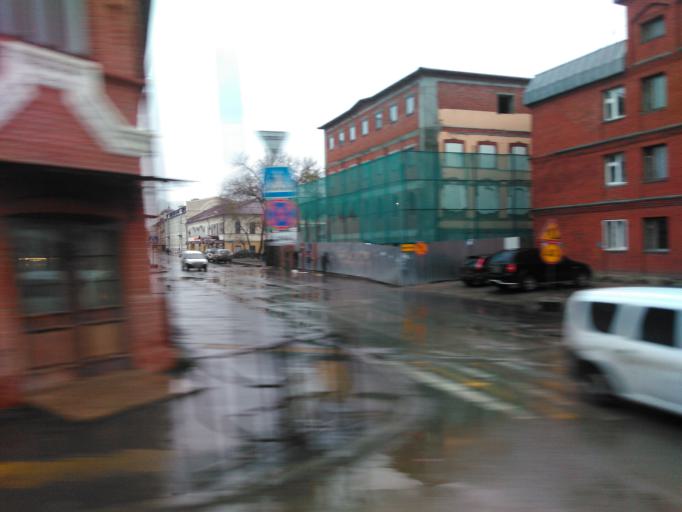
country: RU
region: Tatarstan
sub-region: Gorod Kazan'
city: Kazan
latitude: 55.7844
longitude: 49.1091
